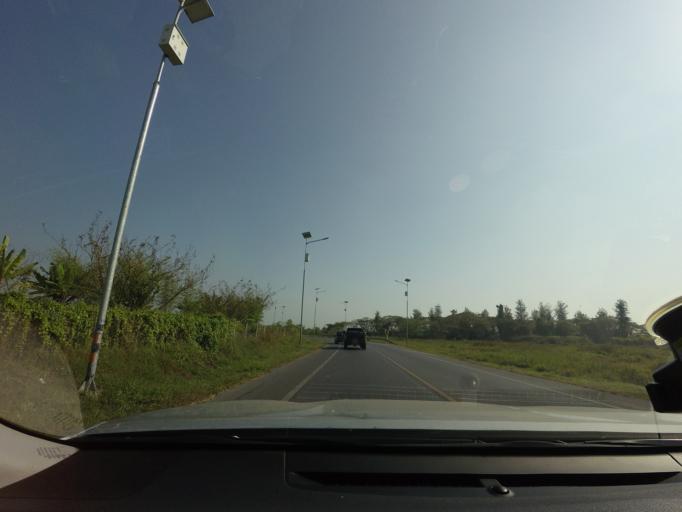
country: TH
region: Nakhon Si Thammarat
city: Nakhon Si Thammarat
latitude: 8.4562
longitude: 99.9801
